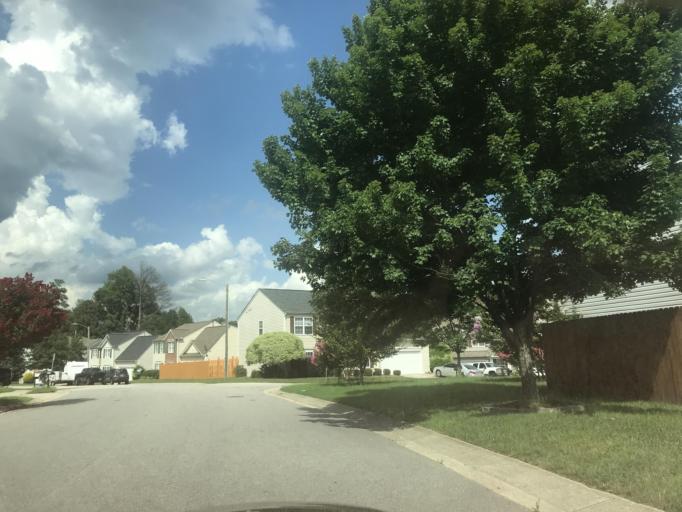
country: US
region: North Carolina
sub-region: Wake County
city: Knightdale
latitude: 35.8393
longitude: -78.5584
